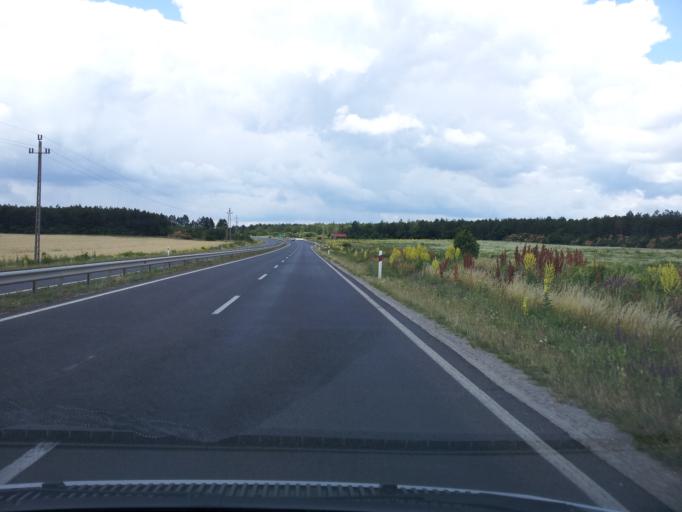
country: HU
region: Veszprem
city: Nemesvamos
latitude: 47.1168
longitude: 17.8430
